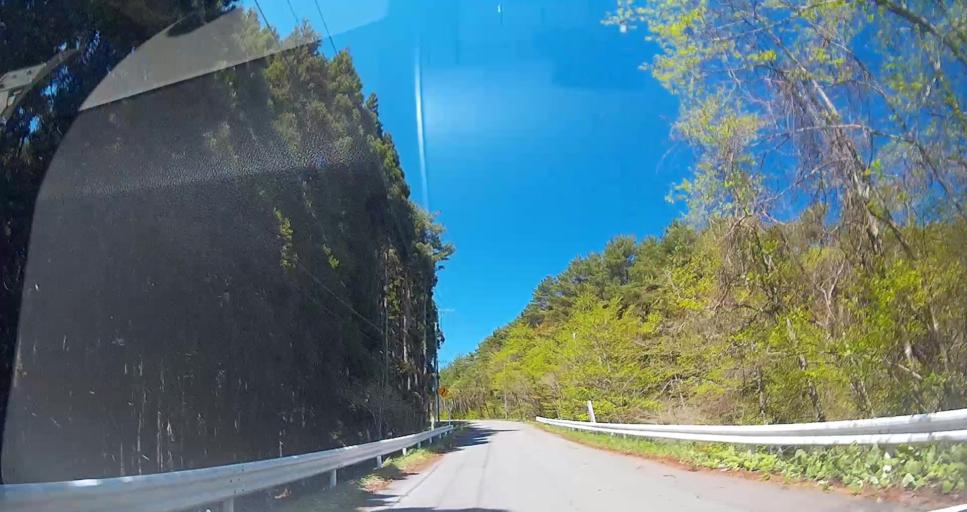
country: JP
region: Aomori
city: Mutsu
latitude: 41.2487
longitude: 141.3929
